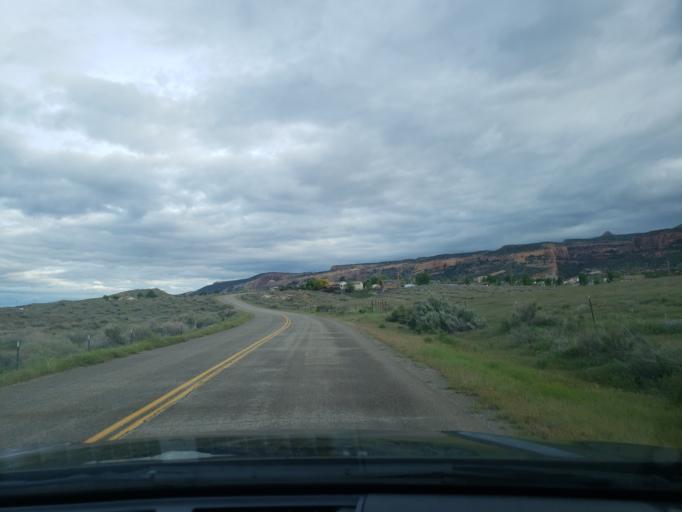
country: US
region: Colorado
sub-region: Mesa County
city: Fruita
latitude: 39.1422
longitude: -108.7442
